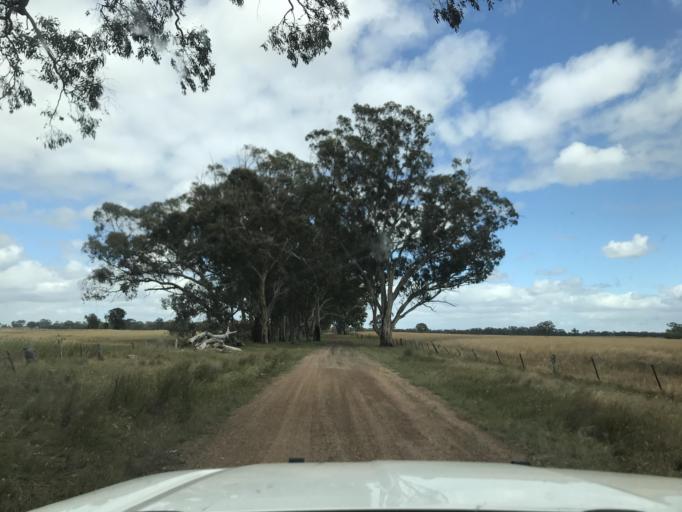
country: AU
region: South Australia
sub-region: Naracoorte and Lucindale
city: Naracoorte
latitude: -36.8985
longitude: 141.3823
